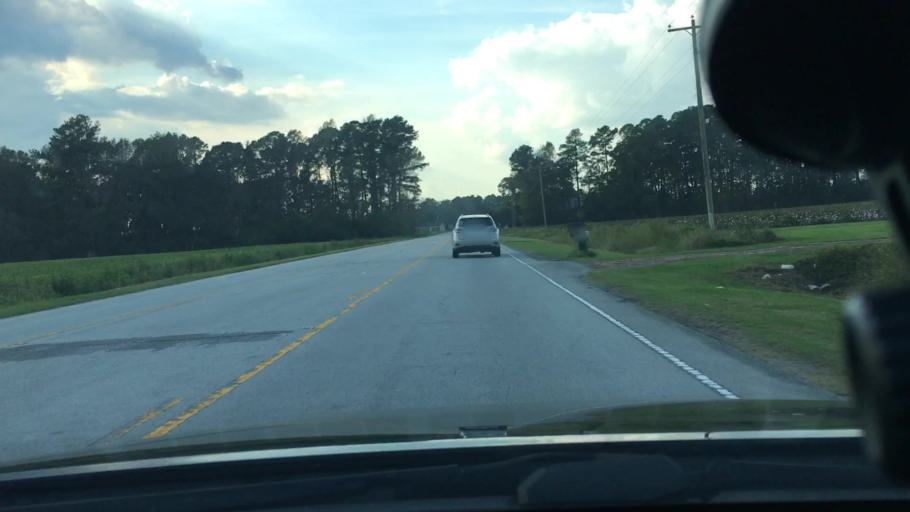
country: US
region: North Carolina
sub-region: Craven County
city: Vanceboro
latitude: 35.3792
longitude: -77.2192
